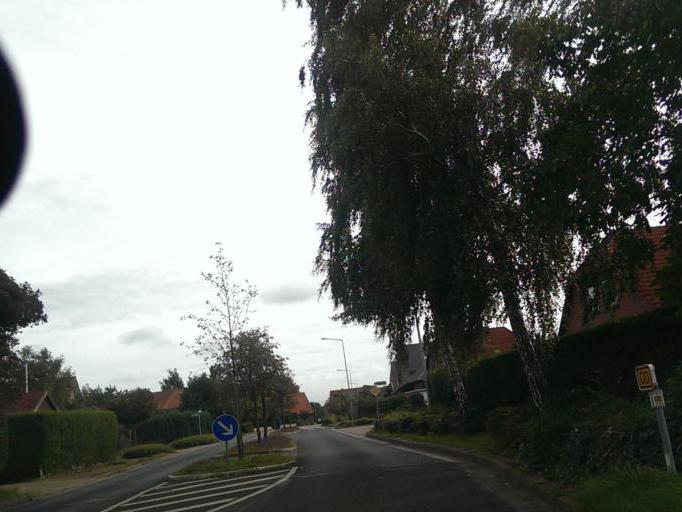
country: DE
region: Lower Saxony
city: Neustadt am Rubenberge
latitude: 52.4580
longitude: 9.5177
